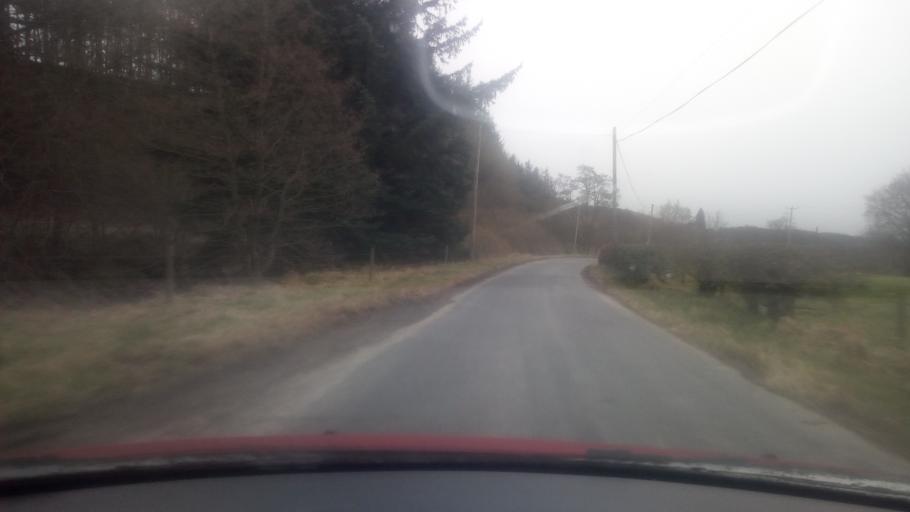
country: GB
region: Scotland
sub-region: The Scottish Borders
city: Jedburgh
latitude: 55.3895
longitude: -2.6537
